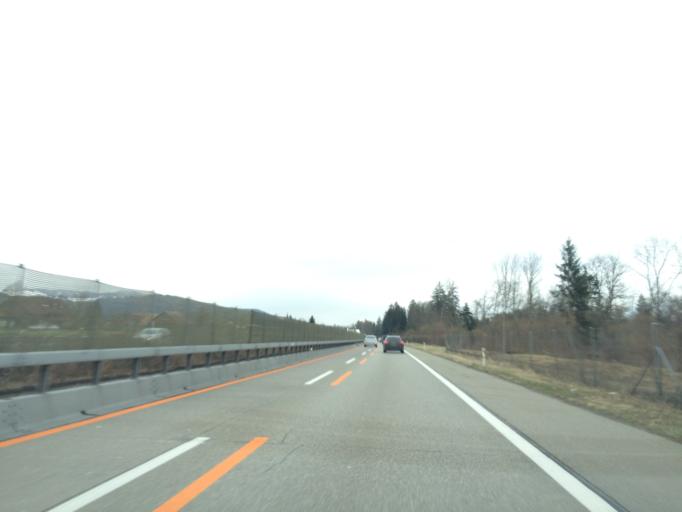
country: CH
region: Bern
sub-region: Bern-Mittelland District
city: Niederwichtrach
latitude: 46.8317
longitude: 7.5638
